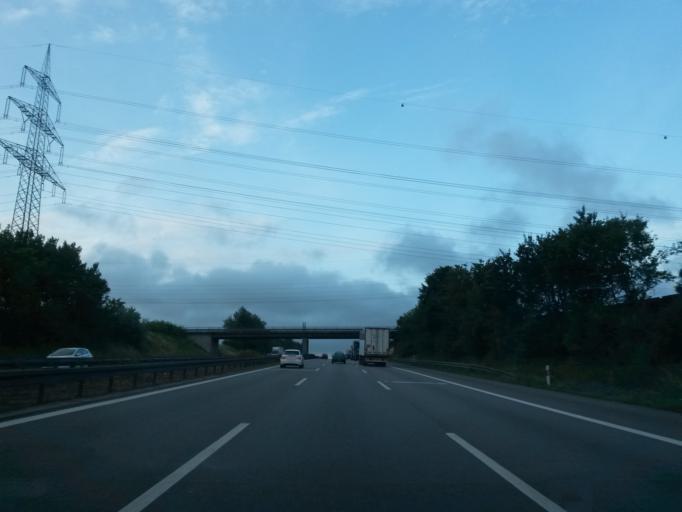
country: DE
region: Bavaria
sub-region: Upper Bavaria
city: Lenting
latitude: 48.8021
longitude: 11.4650
